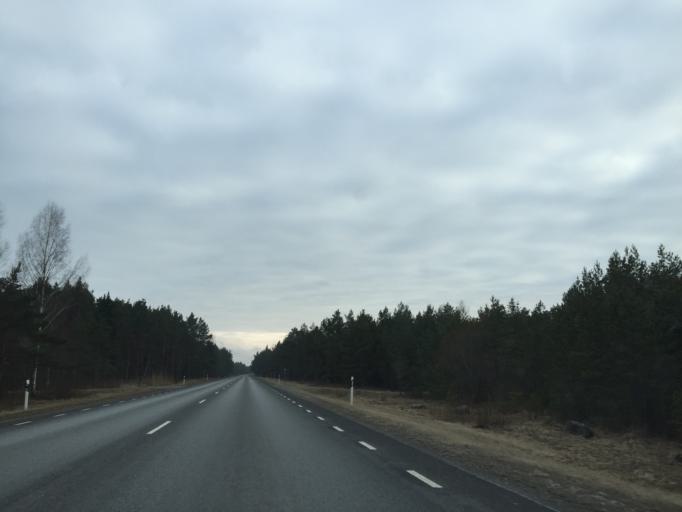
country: EE
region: Saare
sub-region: Orissaare vald
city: Orissaare
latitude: 58.5062
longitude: 22.8689
